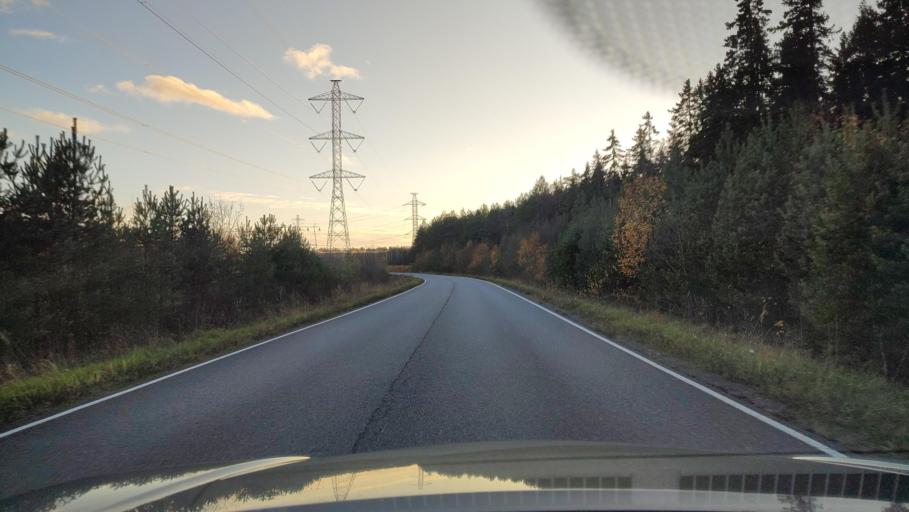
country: FI
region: Ostrobothnia
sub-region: Sydosterbotten
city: Kristinestad
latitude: 62.2838
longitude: 21.3527
